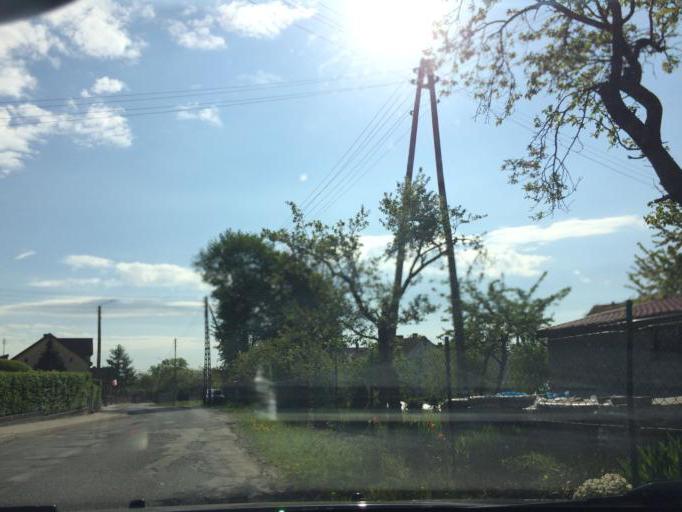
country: PL
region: Lower Silesian Voivodeship
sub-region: Powiat dzierzoniowski
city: Pieszyce
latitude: 50.7523
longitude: 16.5161
